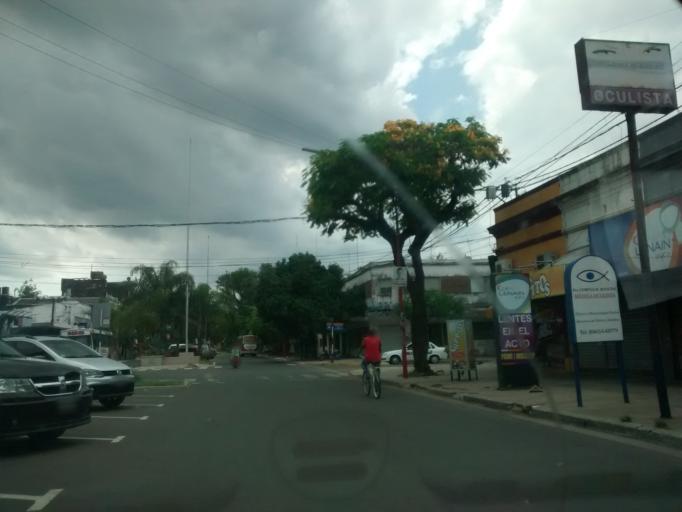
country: AR
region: Chaco
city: Resistencia
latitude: -27.4529
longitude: -58.9845
